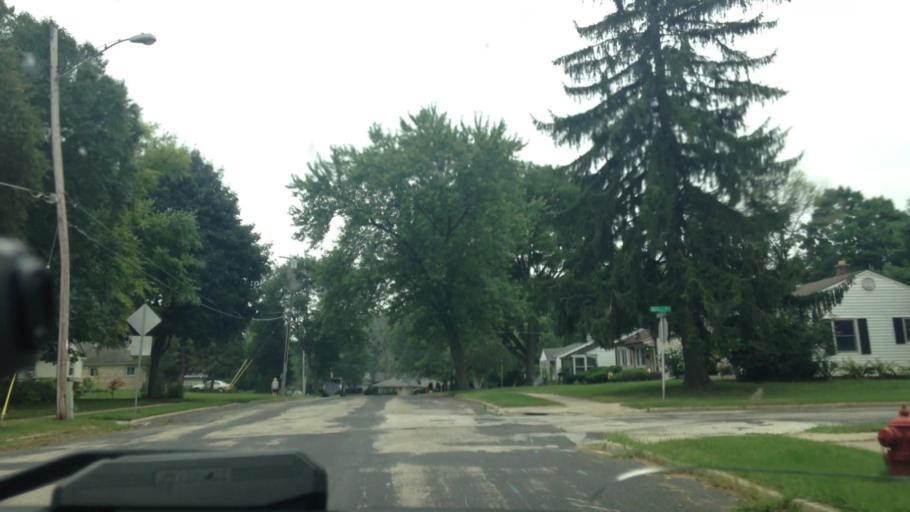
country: US
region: Wisconsin
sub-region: Waukesha County
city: Menomonee Falls
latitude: 43.1748
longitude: -88.1206
